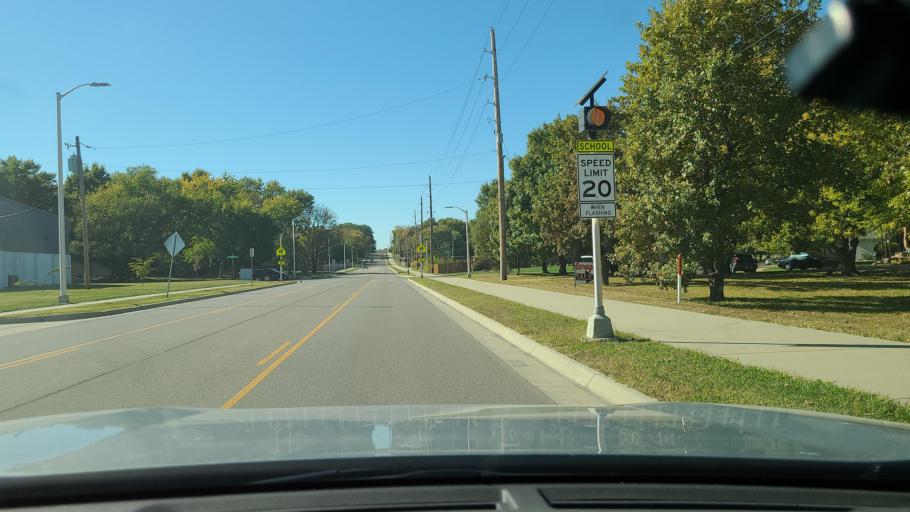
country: US
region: Kansas
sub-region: Shawnee County
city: Topeka
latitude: 39.0006
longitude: -95.7139
